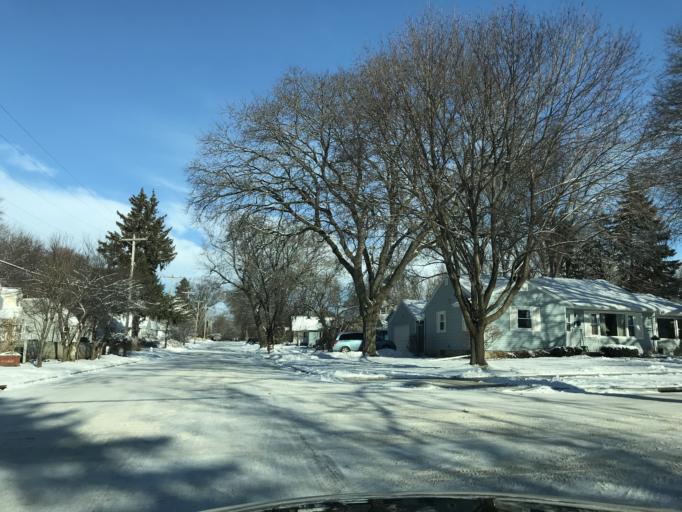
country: US
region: Wisconsin
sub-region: Dane County
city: Monona
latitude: 43.0712
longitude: -89.3130
